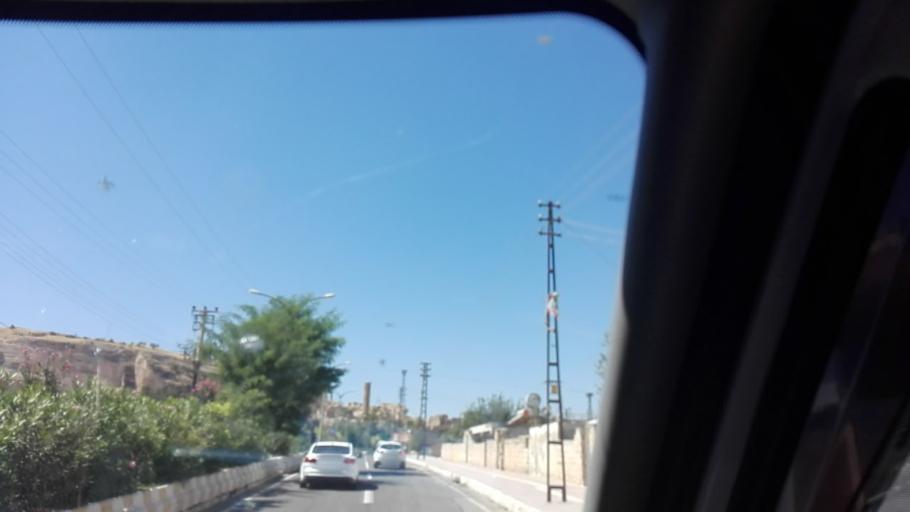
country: TR
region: Batman
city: Hasankeyf
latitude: 37.7130
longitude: 41.4175
